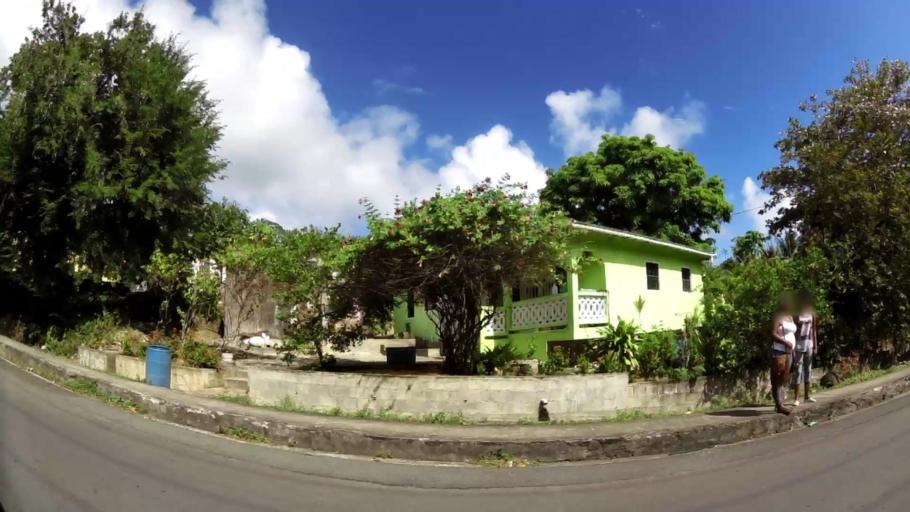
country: LC
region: Dennery Quarter
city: Dennery
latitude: 13.9319
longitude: -60.9056
